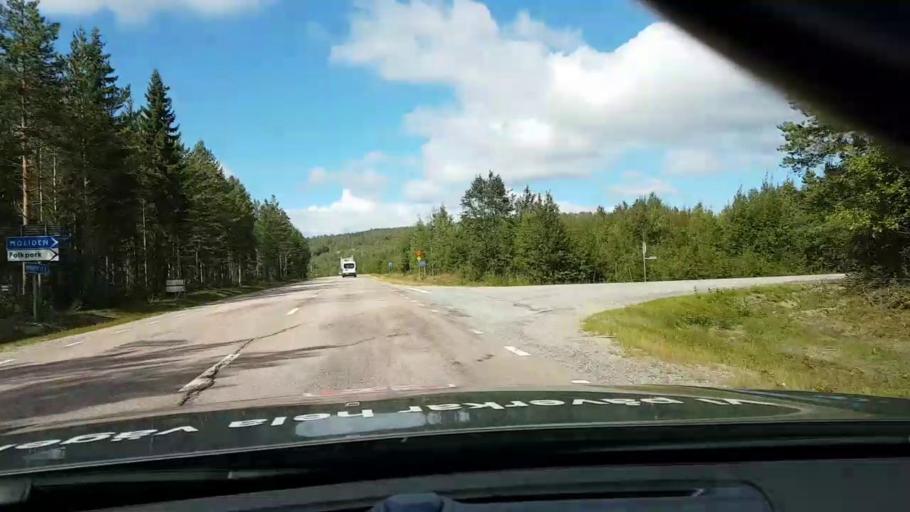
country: SE
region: Vaesternorrland
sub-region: OErnskoeldsviks Kommun
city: Bjasta
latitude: 63.3772
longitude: 18.4241
